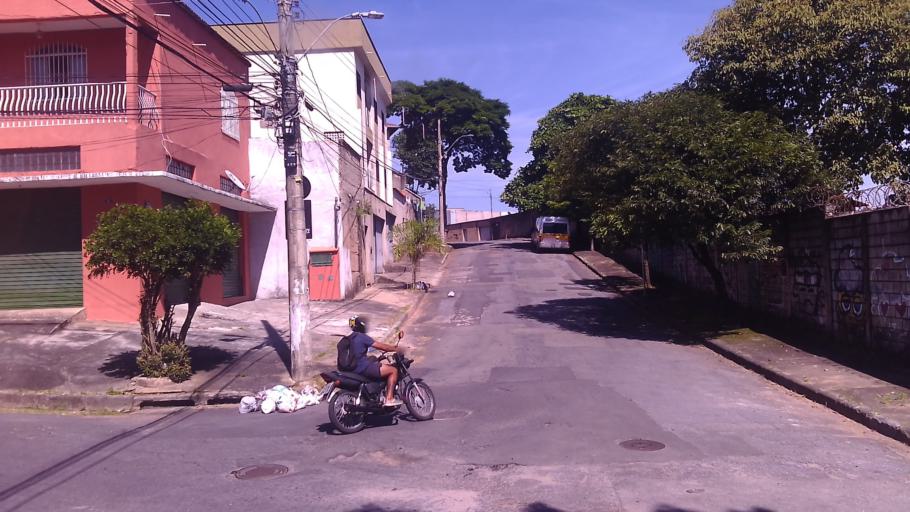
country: BR
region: Minas Gerais
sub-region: Contagem
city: Contagem
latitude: -19.9172
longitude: -43.9996
